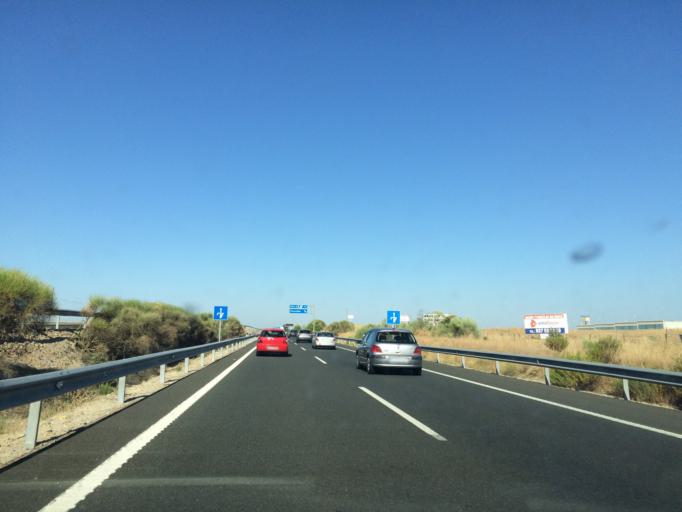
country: ES
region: Extremadura
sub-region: Provincia de Caceres
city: Peraleda de la Mata
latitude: 39.8912
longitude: -5.4169
